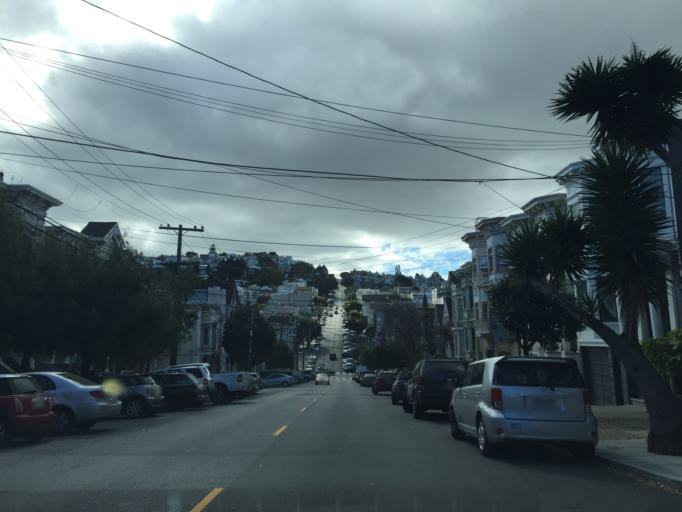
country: US
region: California
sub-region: San Francisco County
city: San Francisco
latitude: 37.7624
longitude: -122.4329
